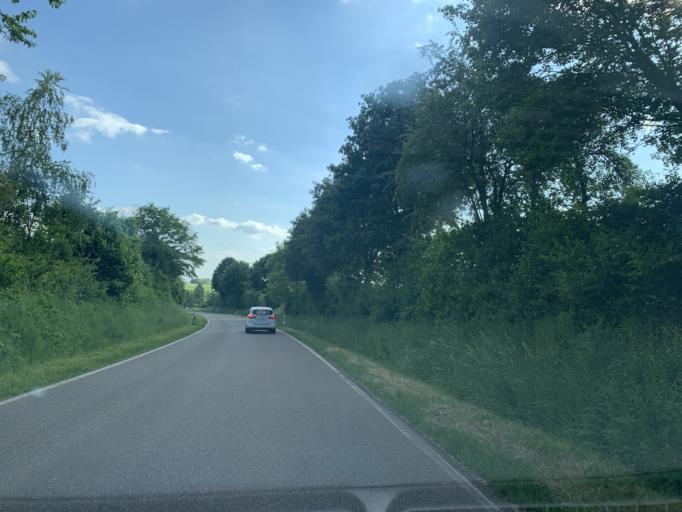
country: DE
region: Baden-Wuerttemberg
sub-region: Tuebingen Region
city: Huttisheim
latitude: 48.2941
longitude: 9.9369
